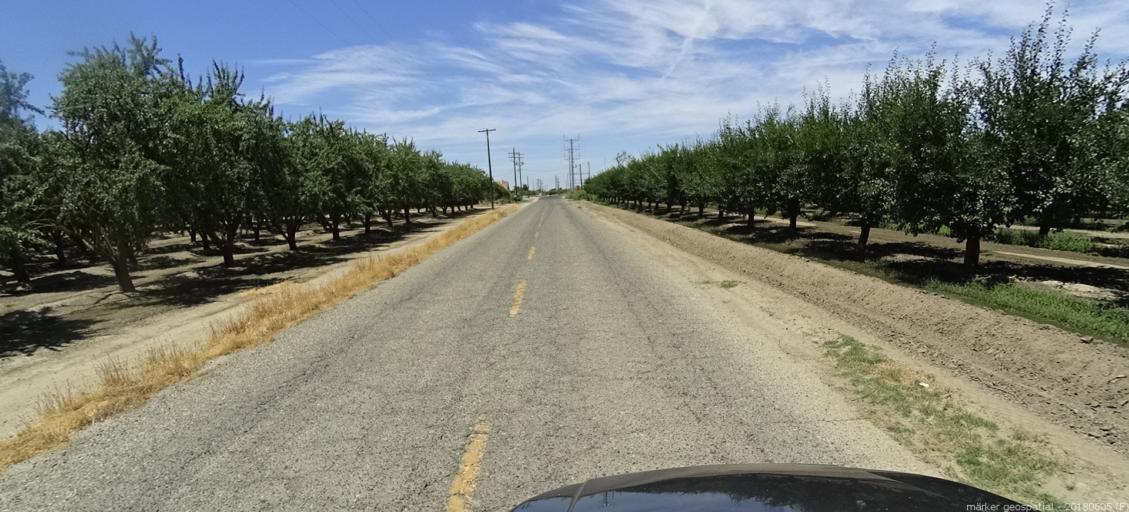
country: US
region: California
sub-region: Madera County
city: Chowchilla
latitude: 37.1200
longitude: -120.3075
